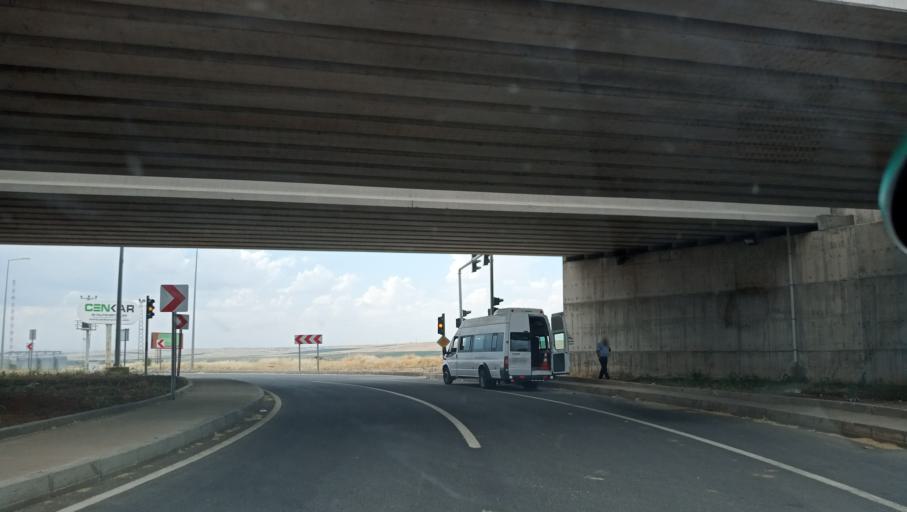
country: TR
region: Diyarbakir
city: Cinar
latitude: 37.8098
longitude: 40.3284
